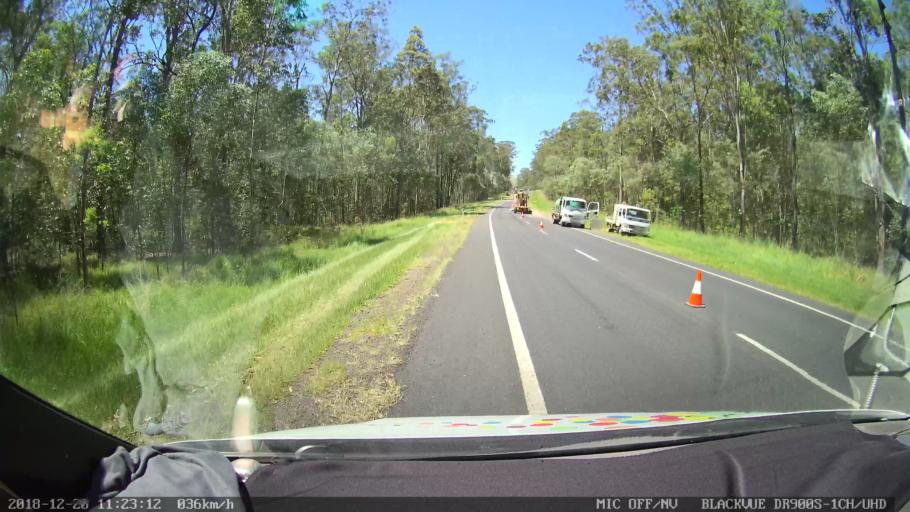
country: AU
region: New South Wales
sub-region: Richmond Valley
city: Casino
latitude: -29.0644
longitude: 153.0046
